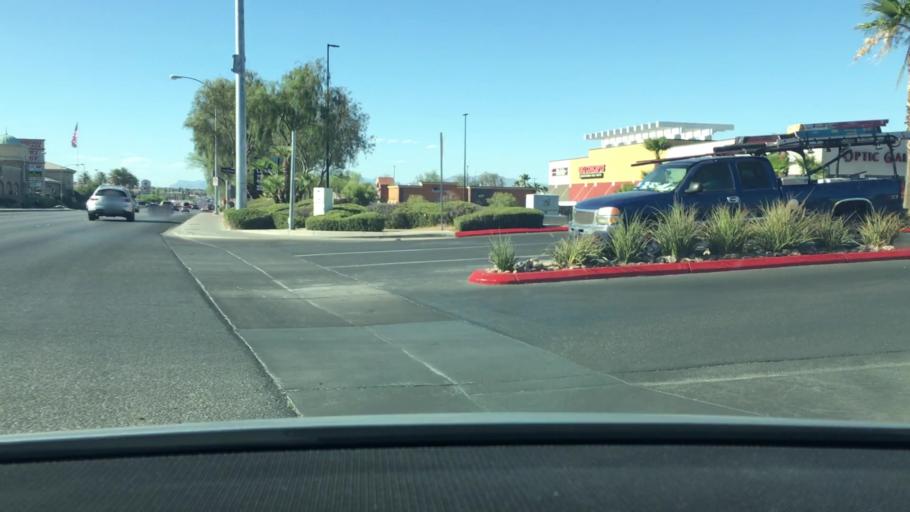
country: US
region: Nevada
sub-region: Clark County
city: Summerlin South
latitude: 36.0962
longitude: -115.2972
